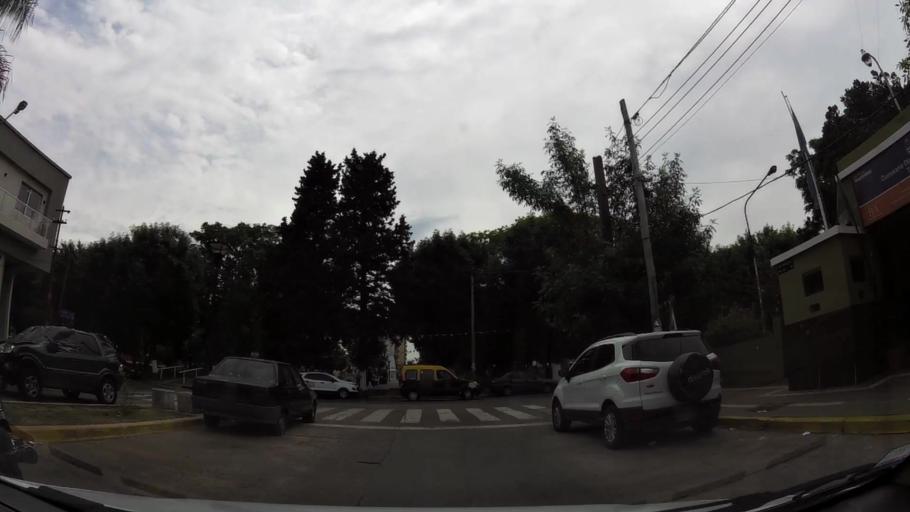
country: AR
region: Buenos Aires F.D.
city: Villa Lugano
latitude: -34.6993
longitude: -58.5082
